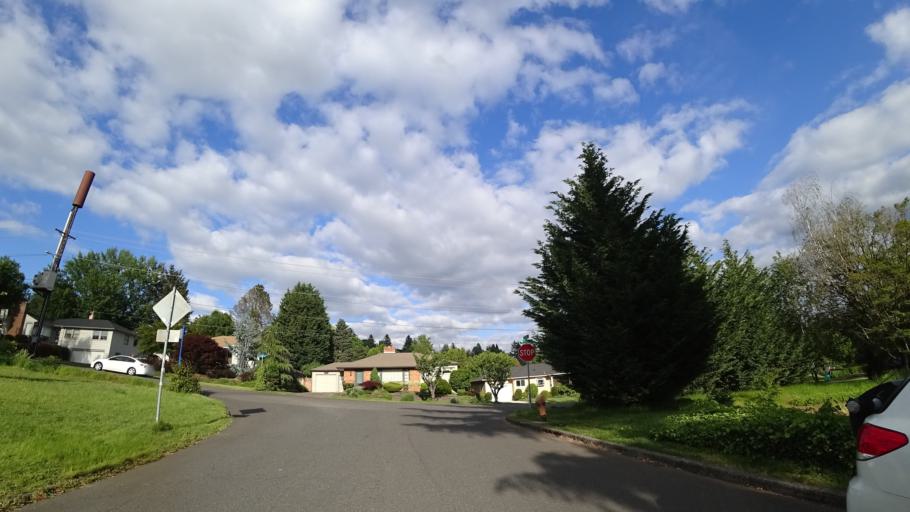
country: US
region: Oregon
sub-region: Washington County
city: Garden Home-Whitford
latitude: 45.4786
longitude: -122.7235
